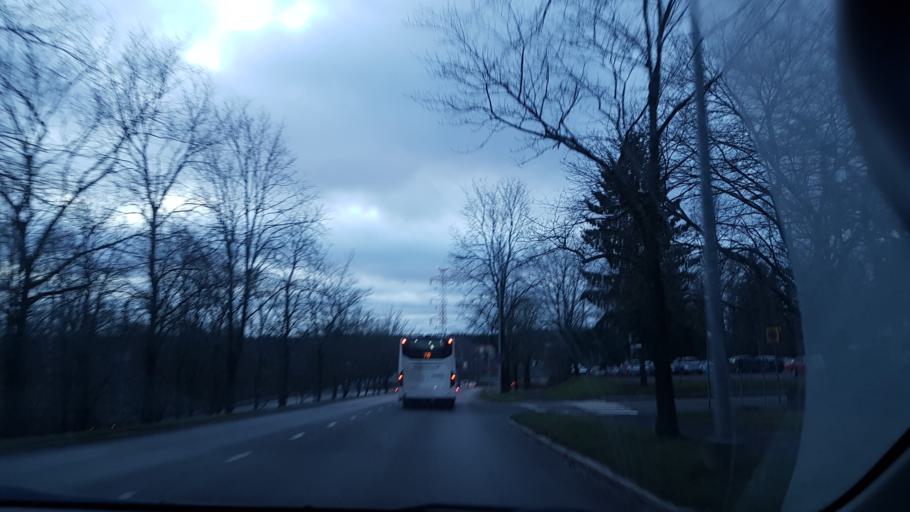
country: FI
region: Uusimaa
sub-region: Helsinki
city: Vantaa
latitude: 60.2721
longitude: 25.1042
